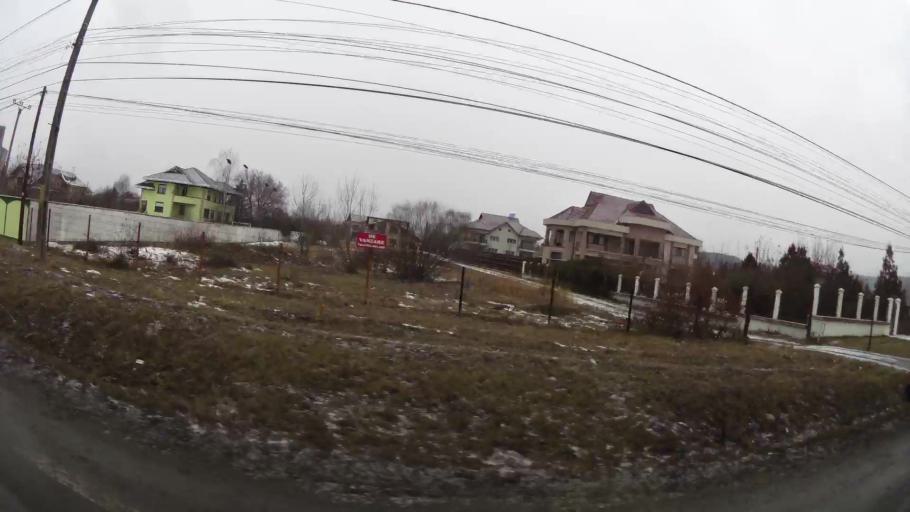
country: RO
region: Dambovita
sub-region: Comuna Aninoasa
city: Viforata
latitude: 44.9487
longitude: 25.4718
